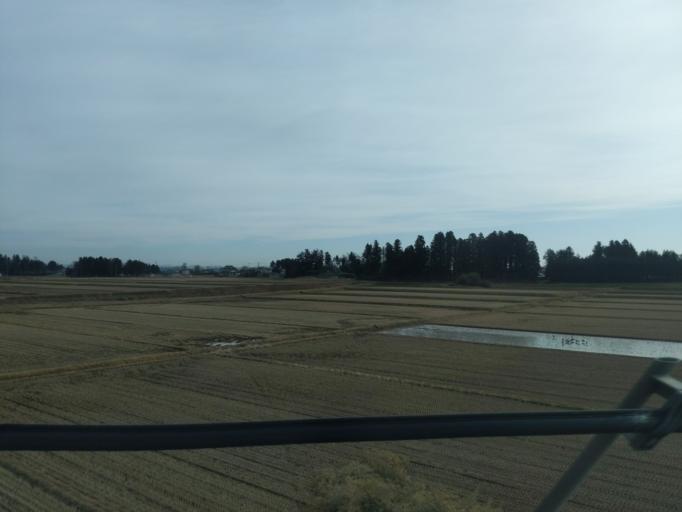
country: JP
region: Iwate
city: Ichinoseki
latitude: 38.7688
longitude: 141.0830
